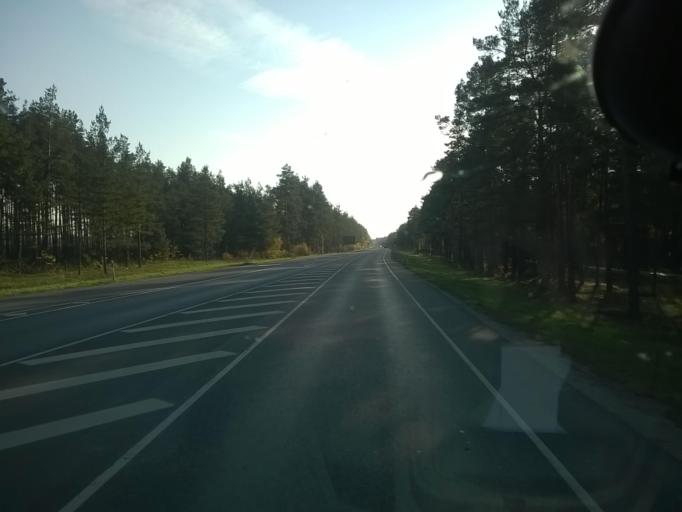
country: EE
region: Harju
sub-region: Saku vald
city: Saku
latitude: 59.3316
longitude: 24.6953
